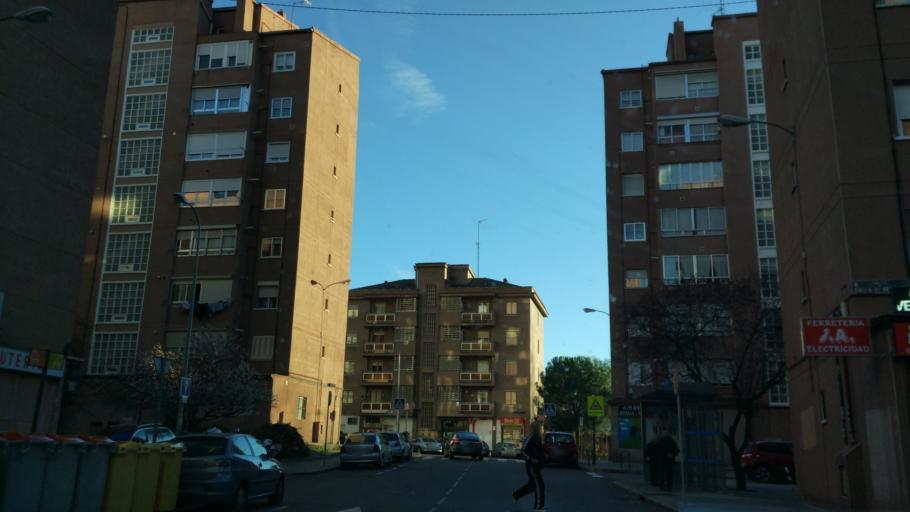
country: ES
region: Madrid
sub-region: Provincia de Madrid
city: Pinar de Chamartin
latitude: 40.4862
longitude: -3.6899
